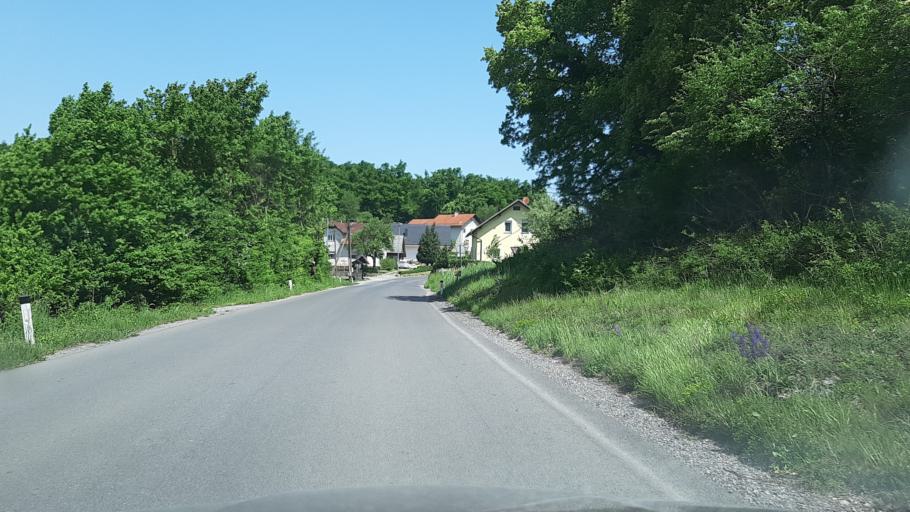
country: SI
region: Brezovica
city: Notranje Gorice
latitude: 45.9606
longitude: 14.3905
